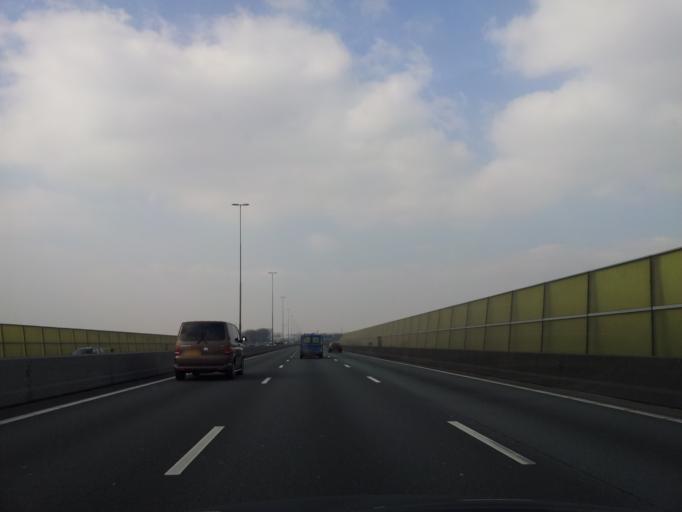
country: NL
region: Gelderland
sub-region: Gemeente Maasdriel
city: Hedel
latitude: 51.7411
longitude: 5.3018
